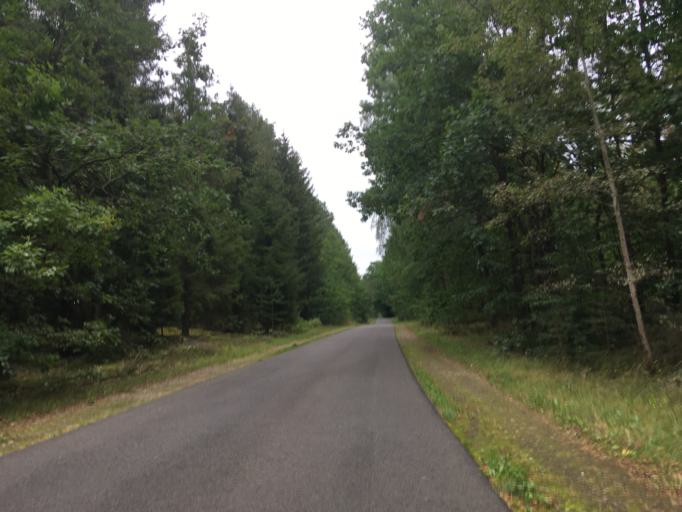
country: DE
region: Brandenburg
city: Templin
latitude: 53.0460
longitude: 13.5169
